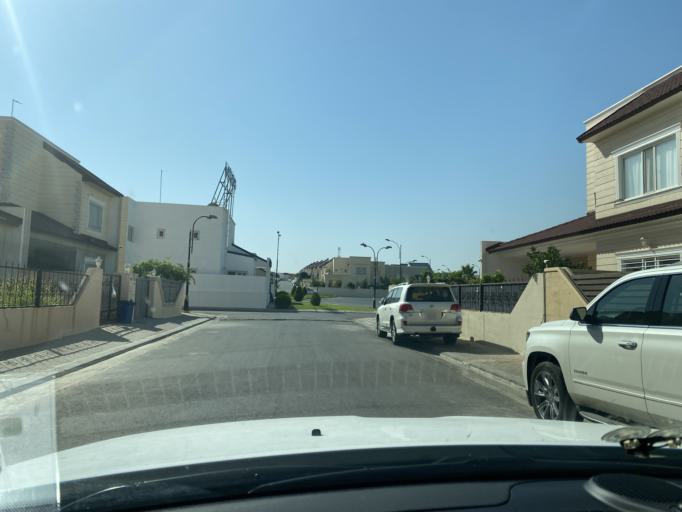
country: IQ
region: Arbil
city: Erbil
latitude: 36.2425
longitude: 44.0507
